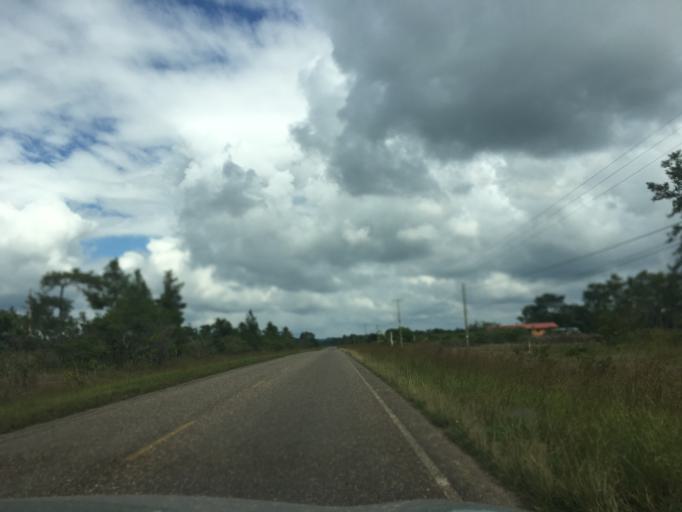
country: BZ
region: Stann Creek
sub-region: Dangriga
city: Dangriga
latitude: 16.8969
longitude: -88.3397
